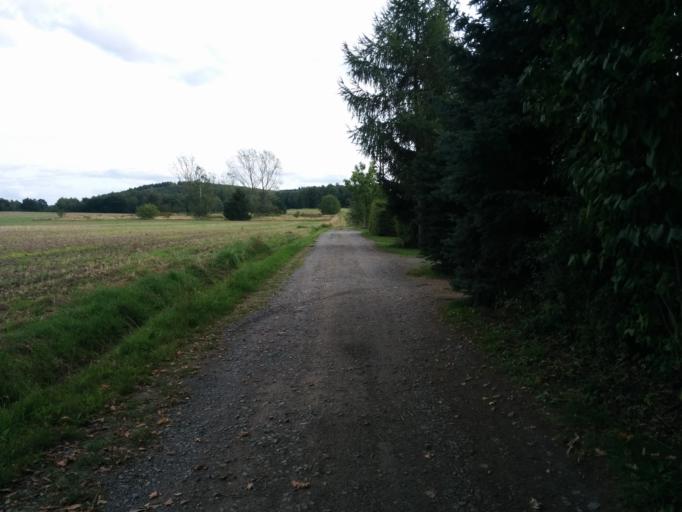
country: DE
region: Saxony
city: Floha
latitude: 50.8524
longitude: 13.0842
